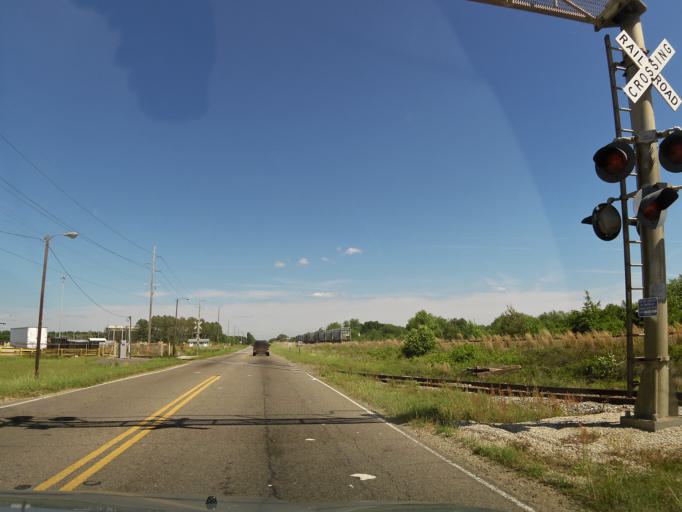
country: US
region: South Carolina
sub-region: Aiken County
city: Aiken
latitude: 33.5433
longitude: -81.6728
